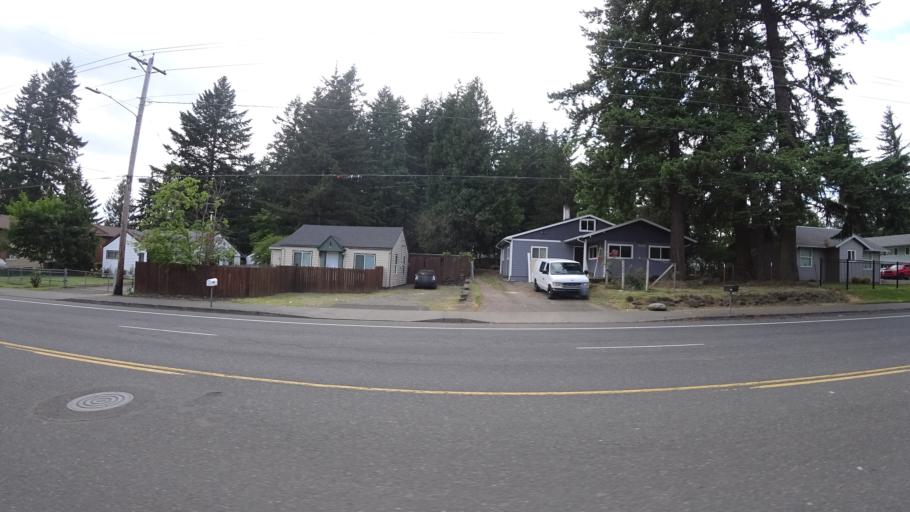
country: US
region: Oregon
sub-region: Multnomah County
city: Fairview
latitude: 45.5248
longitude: -122.4964
